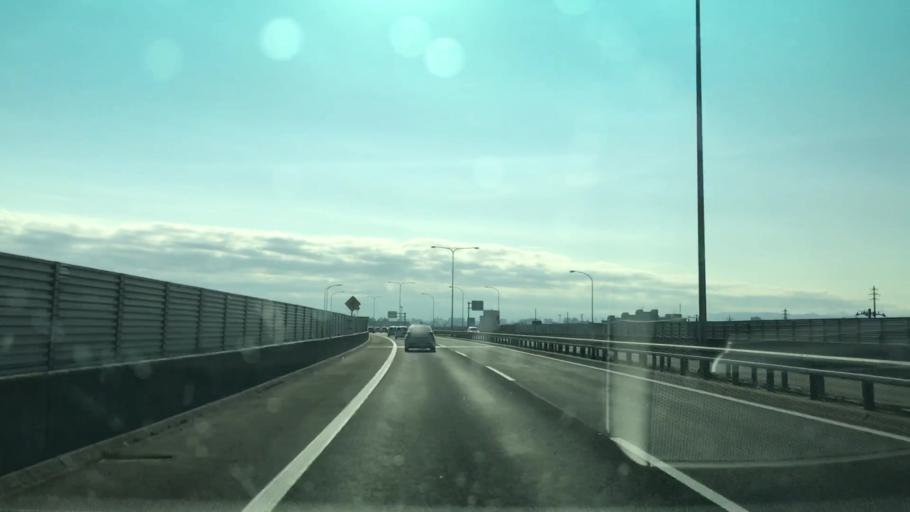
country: JP
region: Hokkaido
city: Sapporo
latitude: 43.0596
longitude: 141.4254
